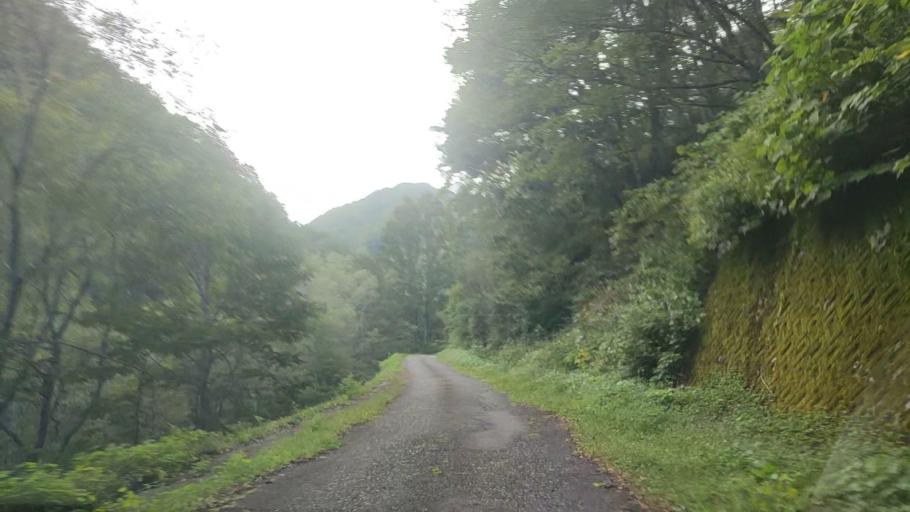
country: JP
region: Toyama
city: Yatsuomachi-higashikumisaka
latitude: 36.3406
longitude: 137.0752
